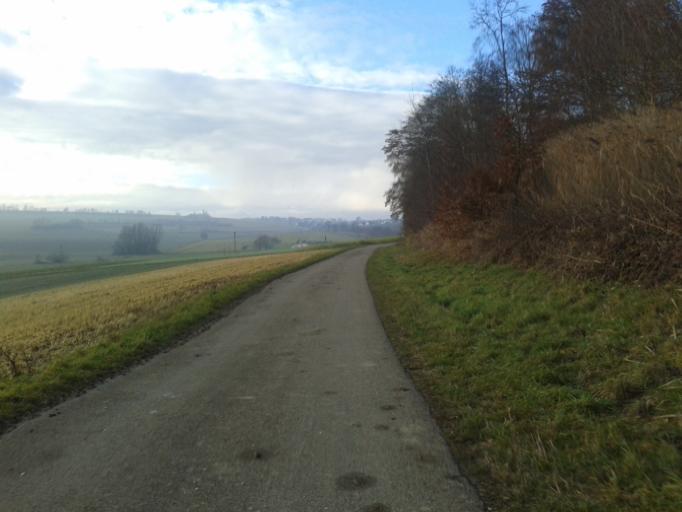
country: DE
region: Baden-Wuerttemberg
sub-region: Tuebingen Region
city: Erbach
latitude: 48.3888
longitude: 9.9146
